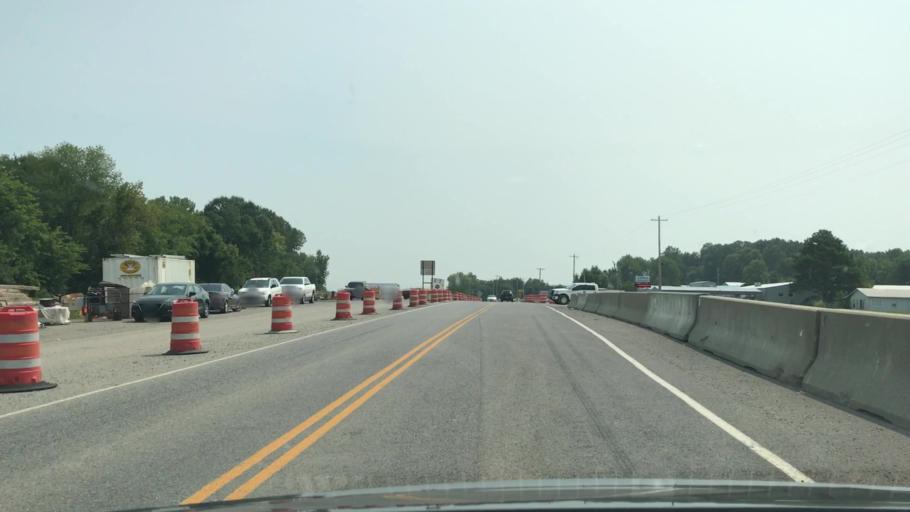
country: US
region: Kentucky
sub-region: Trigg County
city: Cadiz
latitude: 36.7983
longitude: -87.9677
